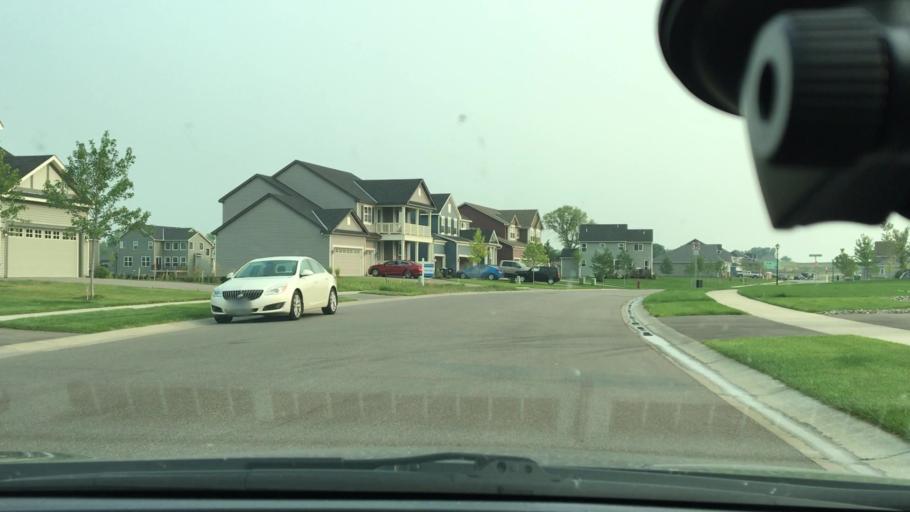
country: US
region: Minnesota
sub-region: Wright County
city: Otsego
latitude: 45.2617
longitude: -93.5713
